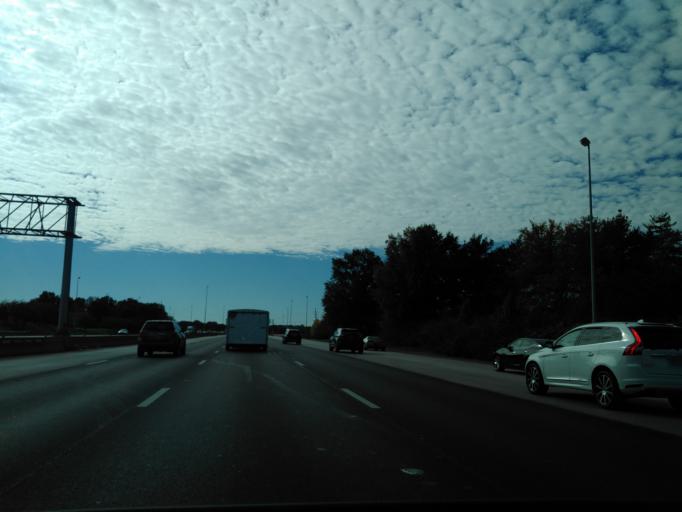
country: US
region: Missouri
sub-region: Saint Louis County
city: Creve Coeur
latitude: 38.6461
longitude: -90.4490
